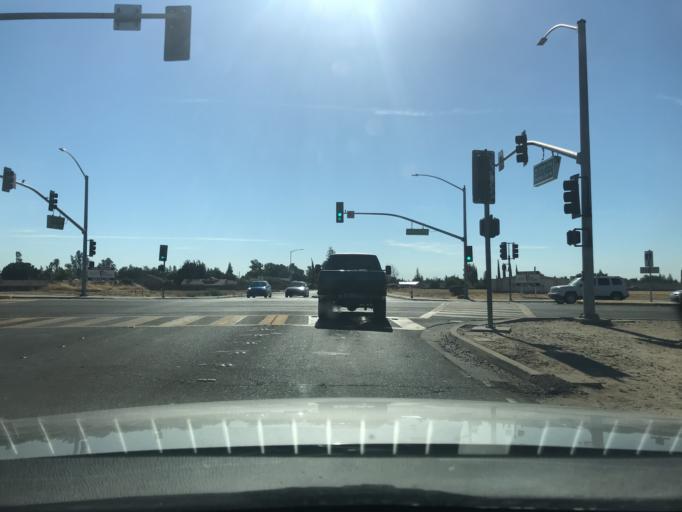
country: US
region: California
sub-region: Merced County
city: Atwater
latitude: 37.3496
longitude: -120.5764
